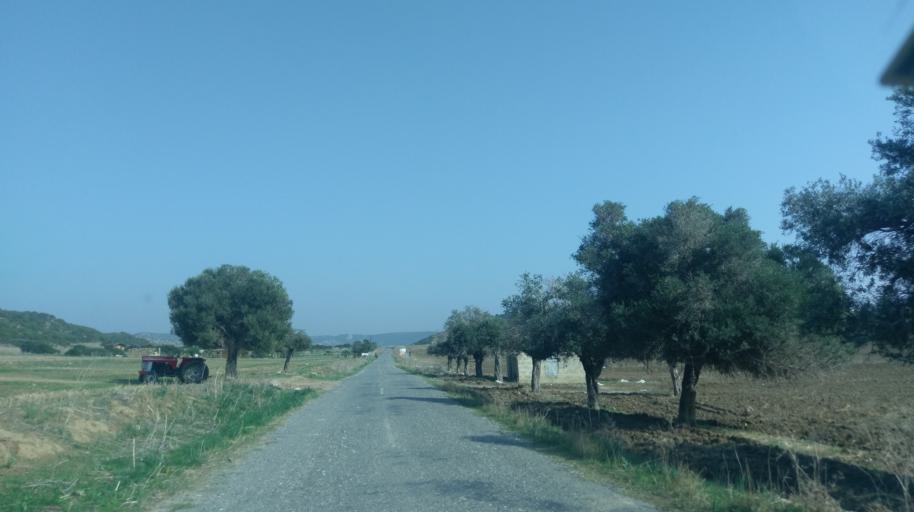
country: CY
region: Ammochostos
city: Rizokarpaso
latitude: 35.6349
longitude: 34.5061
